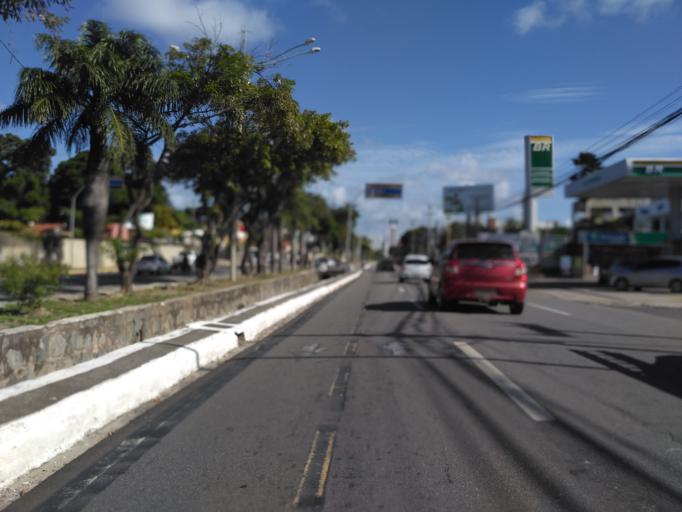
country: BR
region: Pernambuco
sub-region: Jaboatao Dos Guararapes
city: Jaboatao
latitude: -8.1595
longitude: -34.9135
